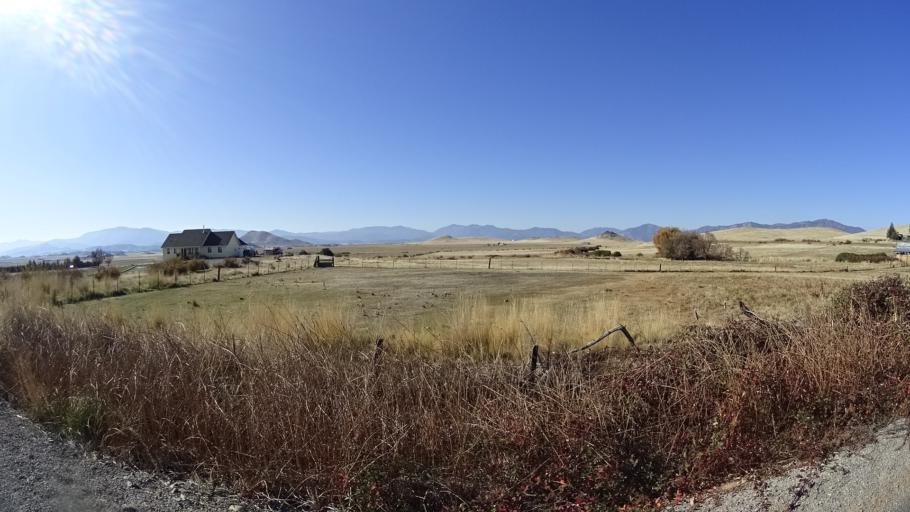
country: US
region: California
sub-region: Siskiyou County
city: Montague
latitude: 41.7362
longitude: -122.4573
